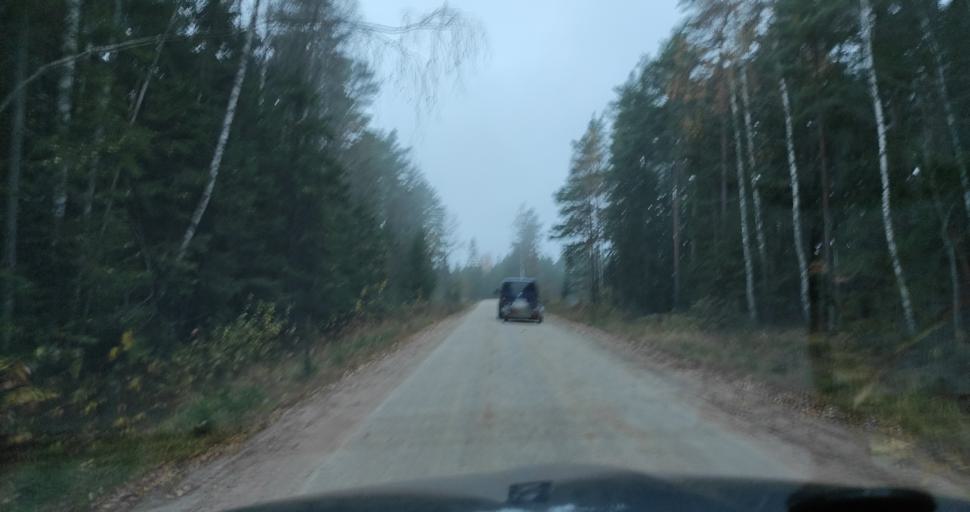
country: LV
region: Pavilostas
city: Pavilosta
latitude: 56.7526
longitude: 21.2663
